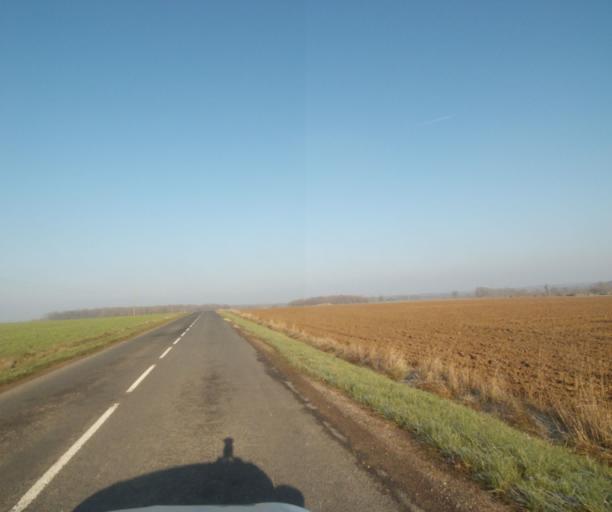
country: FR
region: Champagne-Ardenne
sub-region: Departement de la Haute-Marne
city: Montier-en-Der
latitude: 48.4967
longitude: 4.7534
